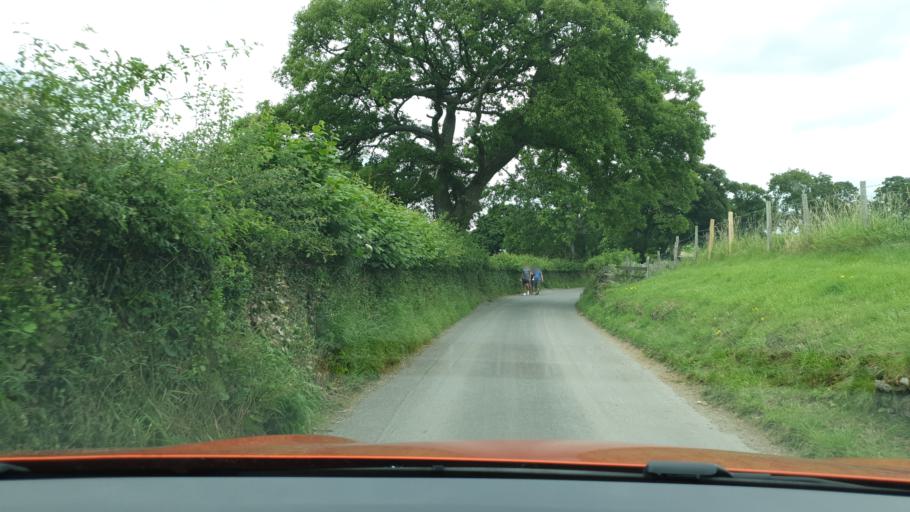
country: GB
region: England
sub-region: Cumbria
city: Penrith
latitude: 54.5958
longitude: -2.8376
